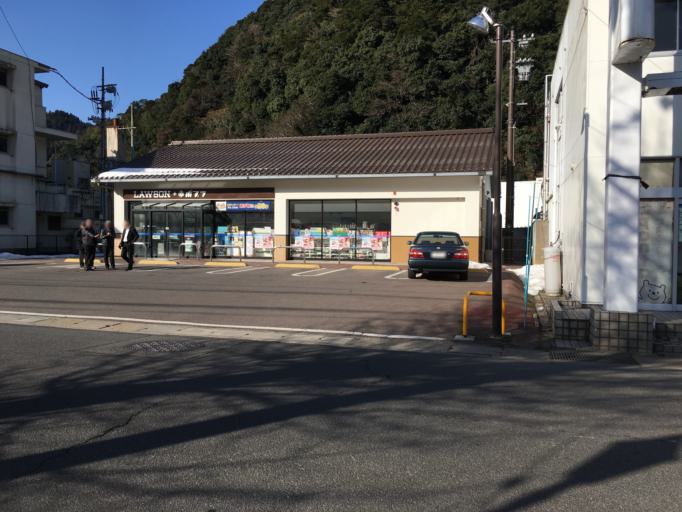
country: JP
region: Shimane
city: Masuda
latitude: 34.4676
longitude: 131.7727
